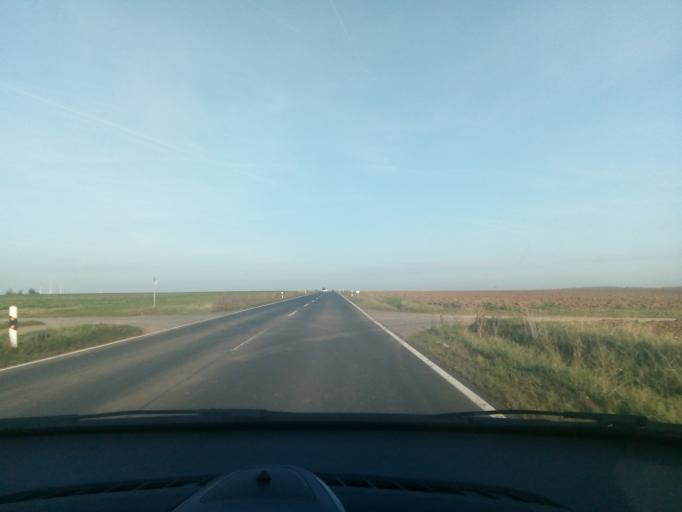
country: DE
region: Bavaria
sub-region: Regierungsbezirk Unterfranken
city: Prosselsheim
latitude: 49.8587
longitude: 10.1106
